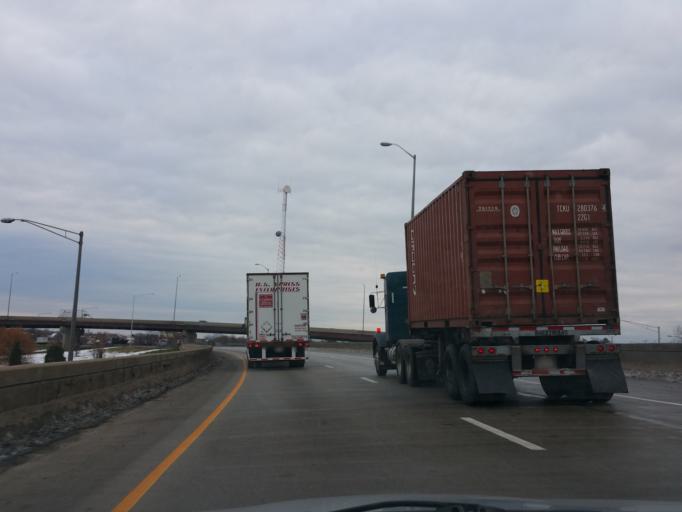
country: US
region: Illinois
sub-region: DuPage County
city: Itasca
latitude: 41.9605
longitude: -88.0267
